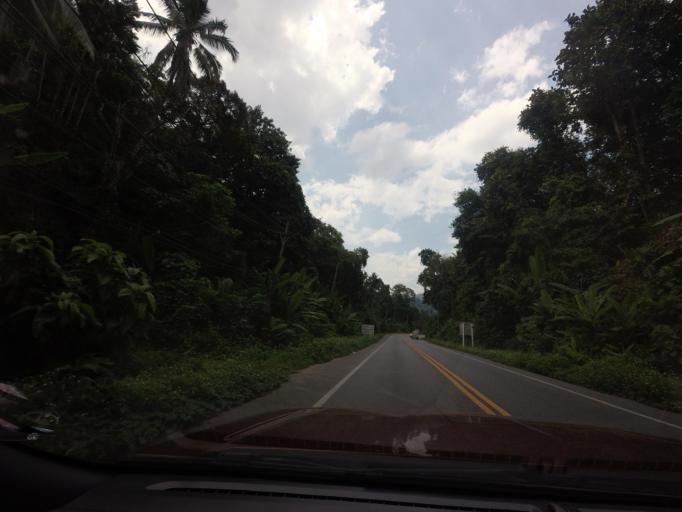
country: TH
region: Yala
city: Than To
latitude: 6.0635
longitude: 101.1949
